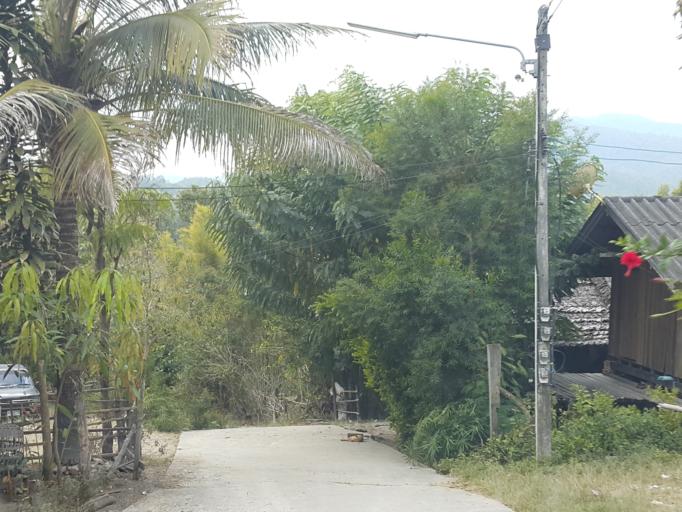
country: TH
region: Chiang Mai
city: Om Koi
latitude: 17.7993
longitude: 98.3346
